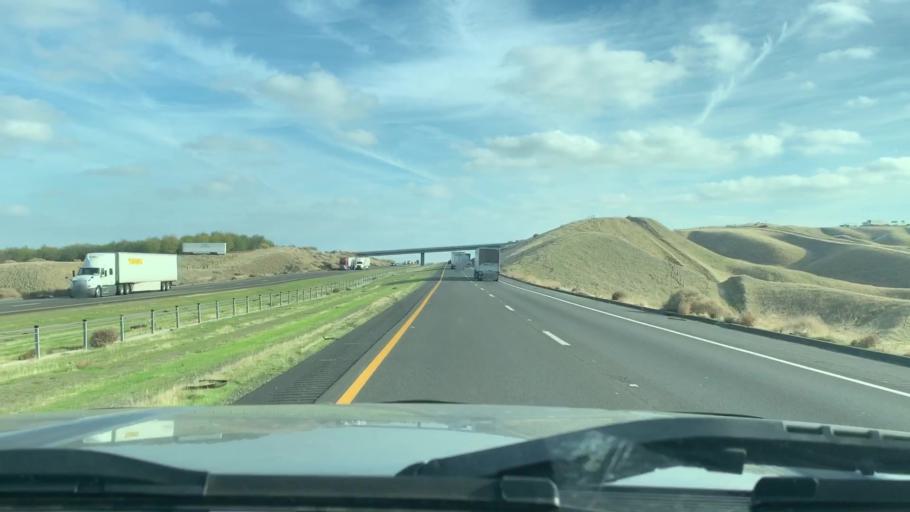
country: US
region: California
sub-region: Kings County
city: Avenal
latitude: 36.0556
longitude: -120.0672
